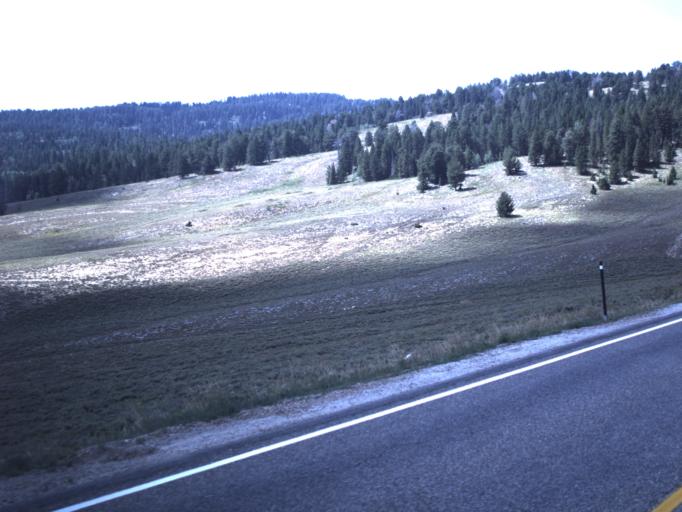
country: US
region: Idaho
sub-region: Bear Lake County
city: Paris
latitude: 41.9320
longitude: -111.4805
